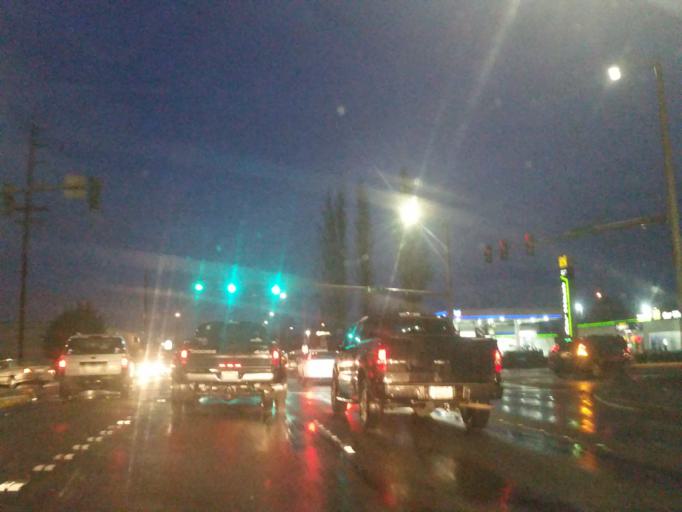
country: US
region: Washington
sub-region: King County
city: Kent
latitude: 47.3818
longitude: -122.2475
